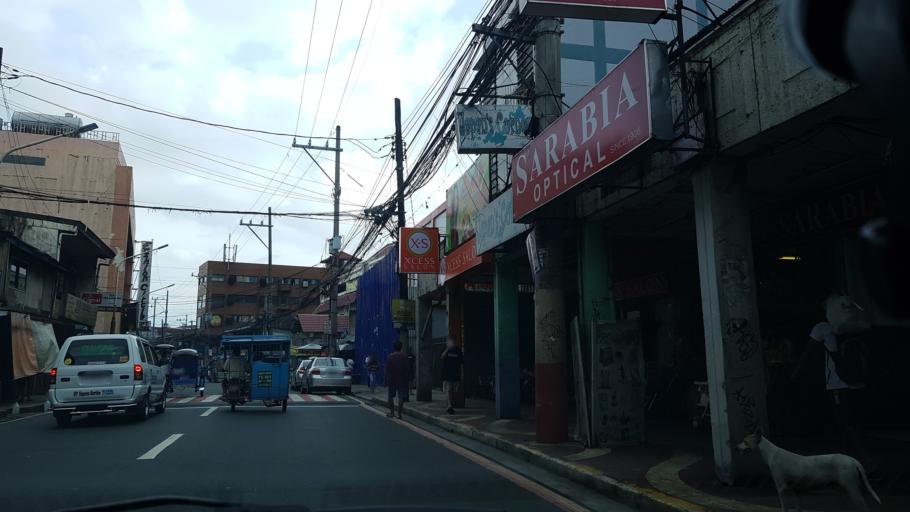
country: PH
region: Calabarzon
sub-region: Province of Rizal
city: Pateros
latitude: 14.5629
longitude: 121.0760
